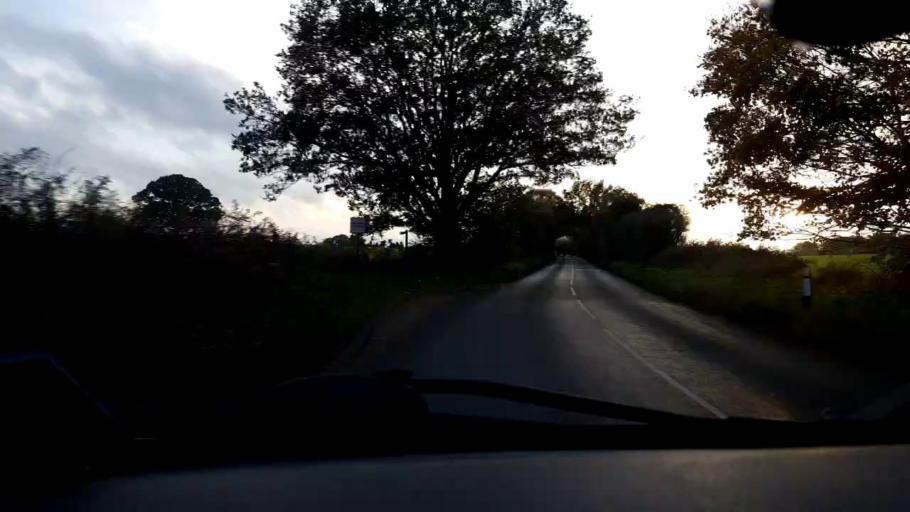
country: GB
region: England
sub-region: Norfolk
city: Mattishall
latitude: 52.7113
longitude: 1.1089
